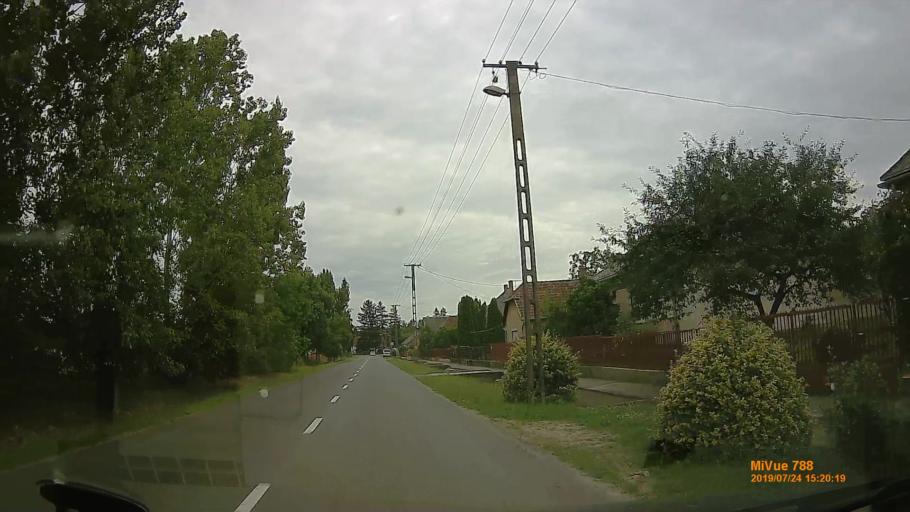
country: HU
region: Szabolcs-Szatmar-Bereg
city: Tarpa
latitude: 48.1636
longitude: 22.5446
